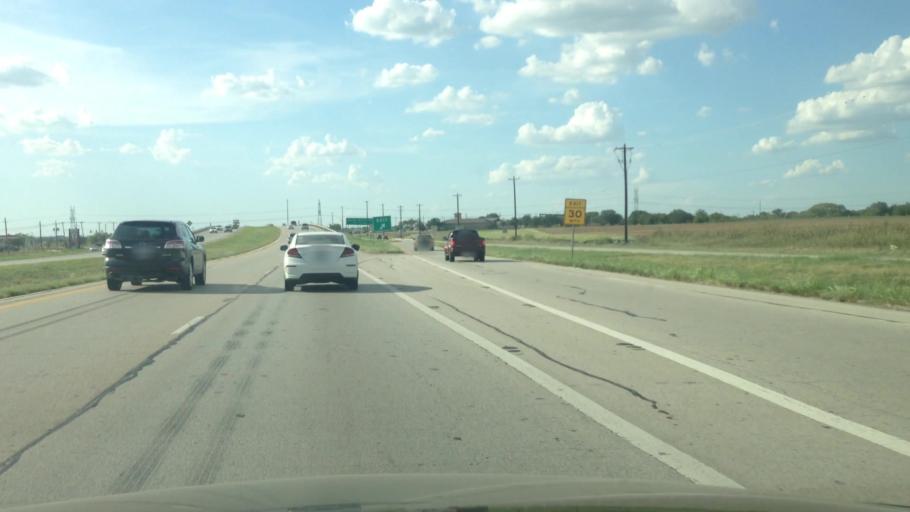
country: US
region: Texas
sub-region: Tarrant County
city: Saginaw
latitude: 32.9141
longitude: -97.3435
